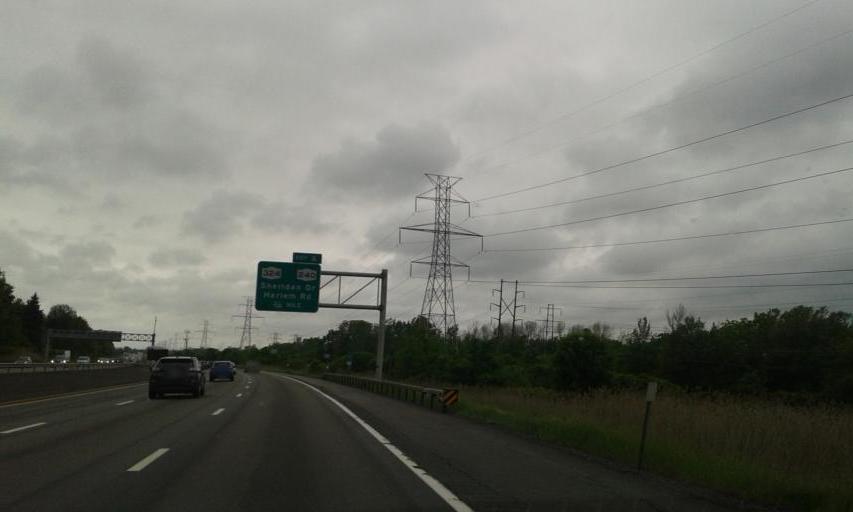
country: US
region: New York
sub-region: Erie County
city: Williamsville
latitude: 42.9679
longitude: -78.7693
